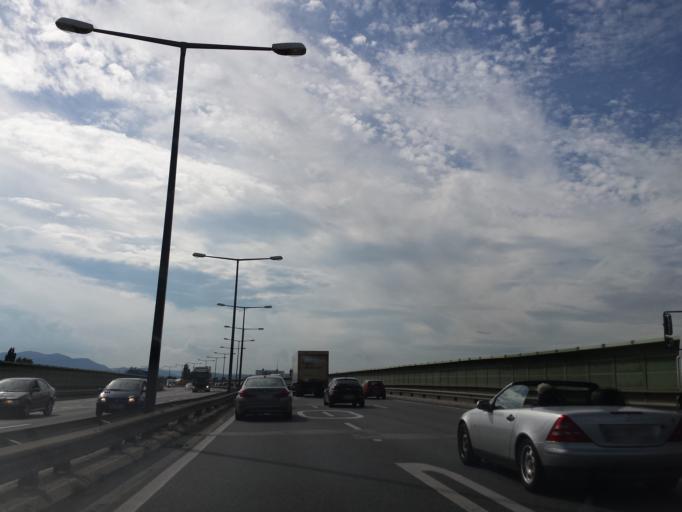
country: AT
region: Lower Austria
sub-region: Politischer Bezirk Modling
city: Vosendorf
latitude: 48.1526
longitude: 16.3520
